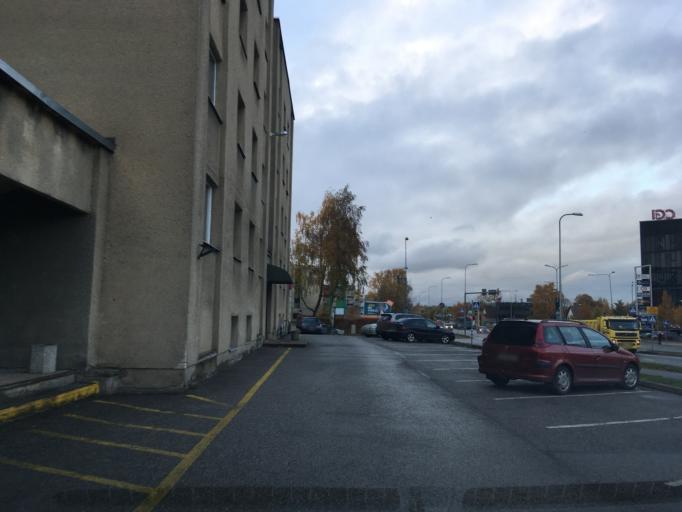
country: EE
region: Tartu
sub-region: Tartu linn
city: Tartu
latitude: 58.3641
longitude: 26.7398
